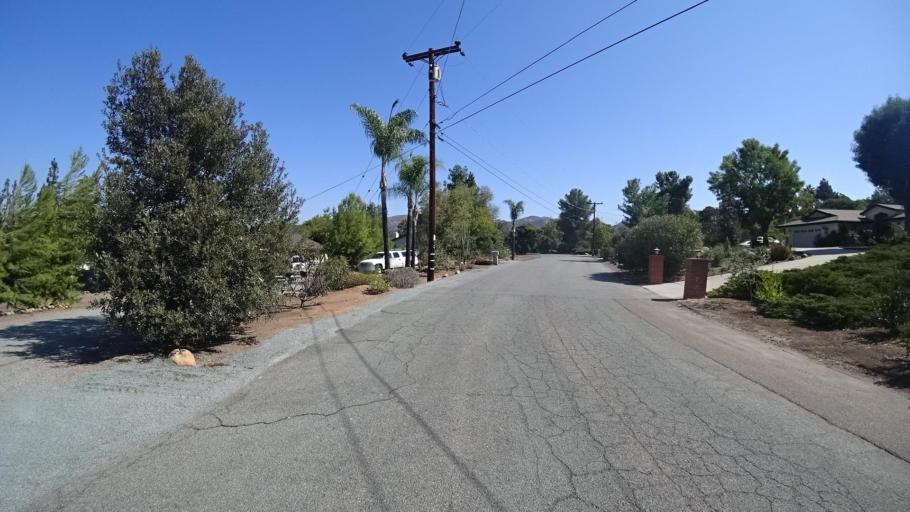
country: US
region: California
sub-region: San Diego County
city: Granite Hills
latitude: 32.7908
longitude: -116.9120
